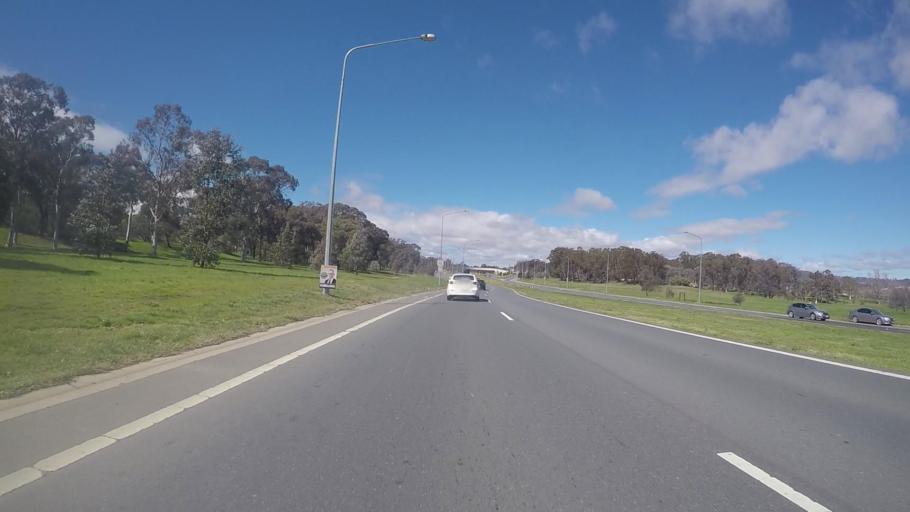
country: AU
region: Australian Capital Territory
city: Canberra
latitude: -35.2954
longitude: 149.1457
